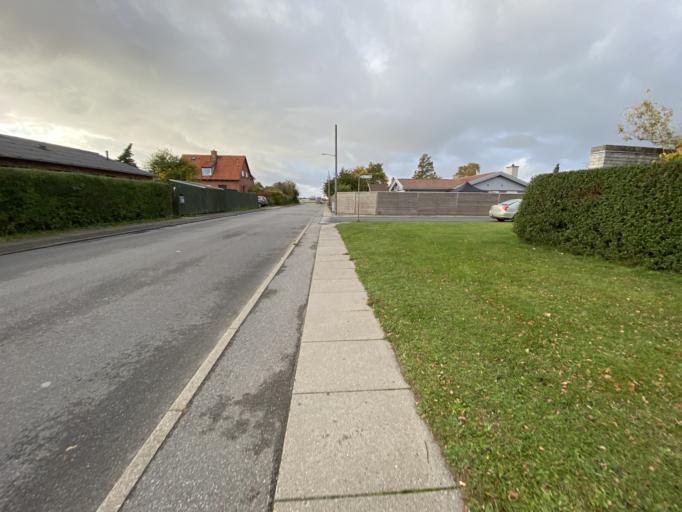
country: DK
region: Capital Region
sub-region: Dragor Kommune
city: Dragor
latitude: 55.5886
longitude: 12.6370
